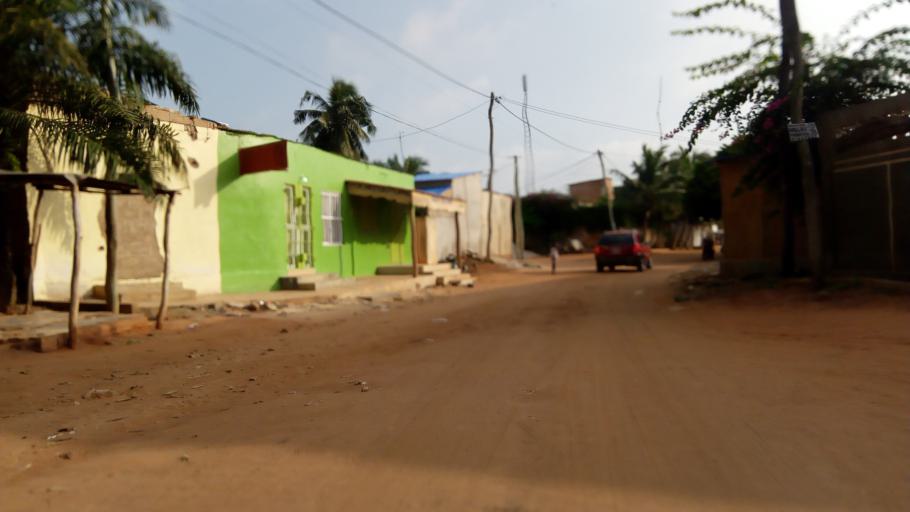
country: TG
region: Maritime
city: Lome
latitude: 6.1748
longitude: 1.1802
